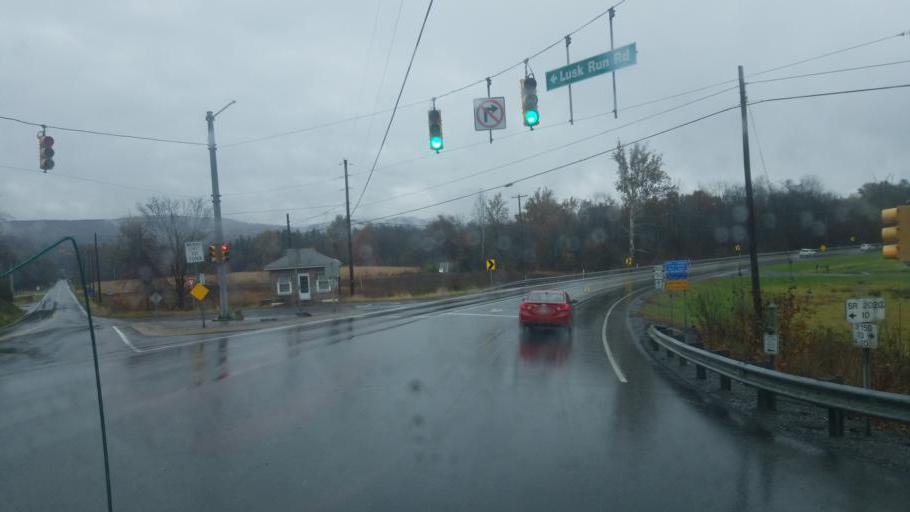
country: US
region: Pennsylvania
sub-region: Clinton County
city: Mill Hall
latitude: 41.1115
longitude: -77.5043
